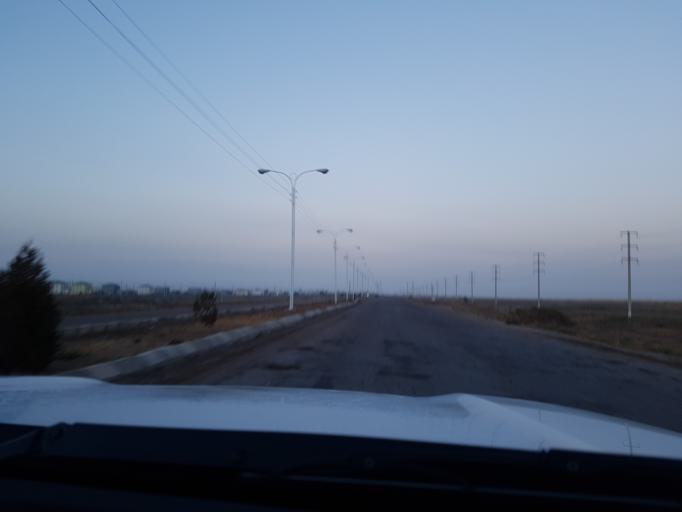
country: TM
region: Dasoguz
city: Koeneuergench
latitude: 41.7426
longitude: 58.7086
